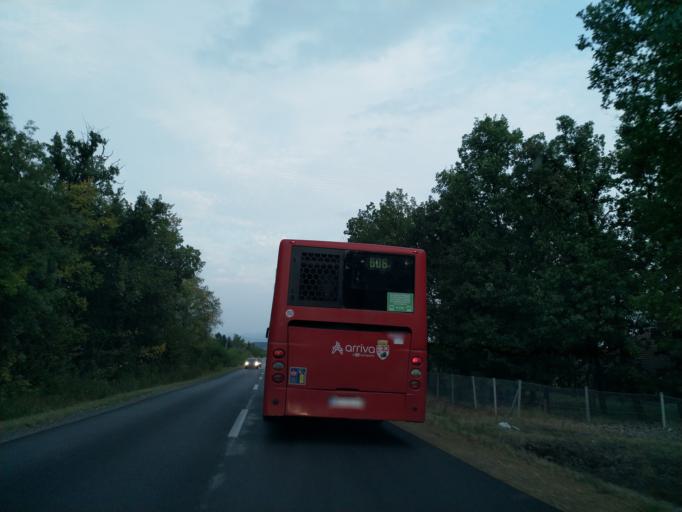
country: RS
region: Central Serbia
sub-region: Sumadijski Okrug
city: Kragujevac
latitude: 44.1252
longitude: 20.8208
